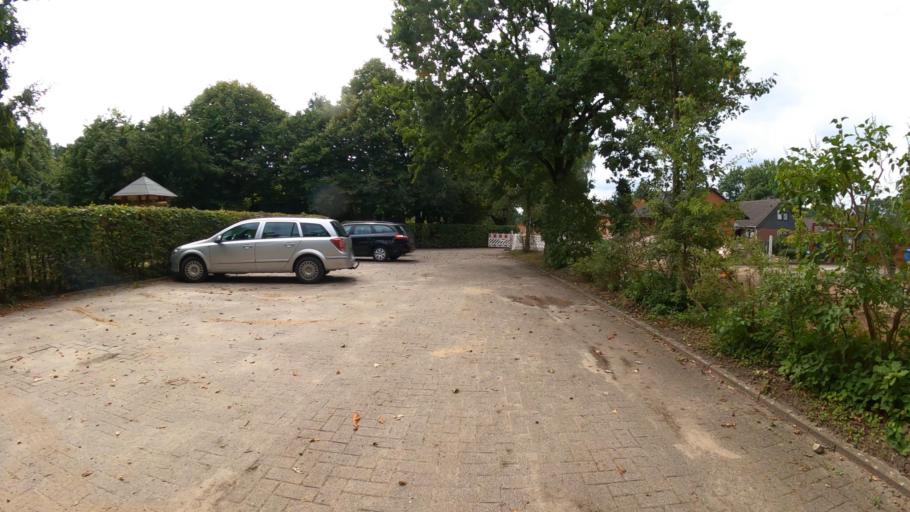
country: DE
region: Lower Saxony
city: Wenzendorf
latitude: 53.3496
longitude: 9.7560
